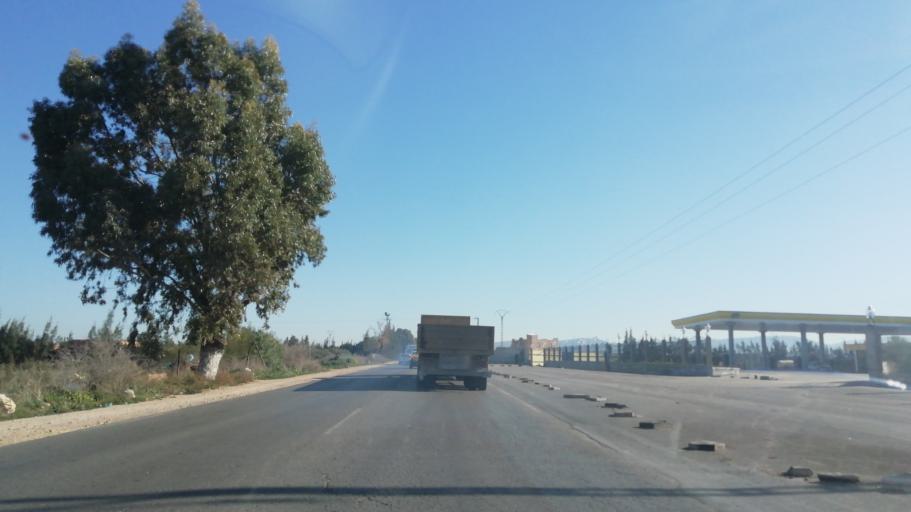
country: DZ
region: Relizane
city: Zemoura
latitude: 35.7468
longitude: 0.6955
